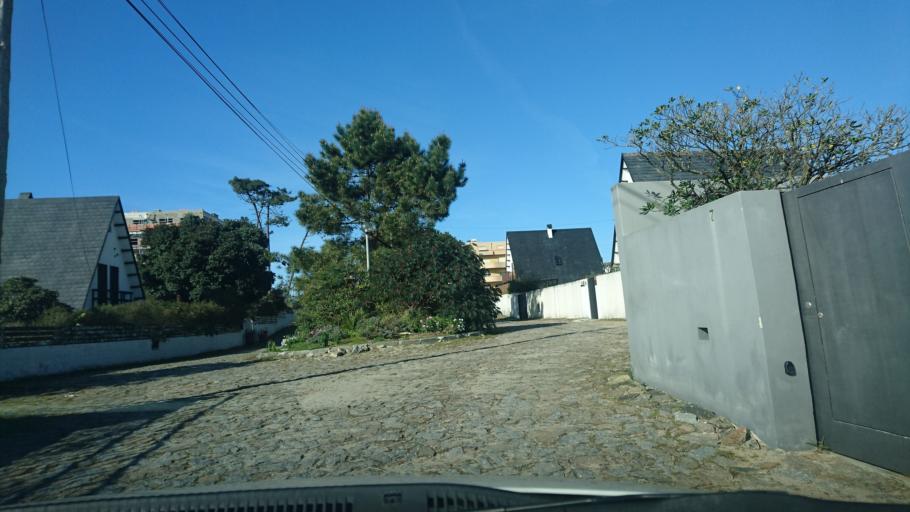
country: PT
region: Aveiro
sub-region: Ovar
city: Esmoriz
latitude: 40.9531
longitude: -8.6495
